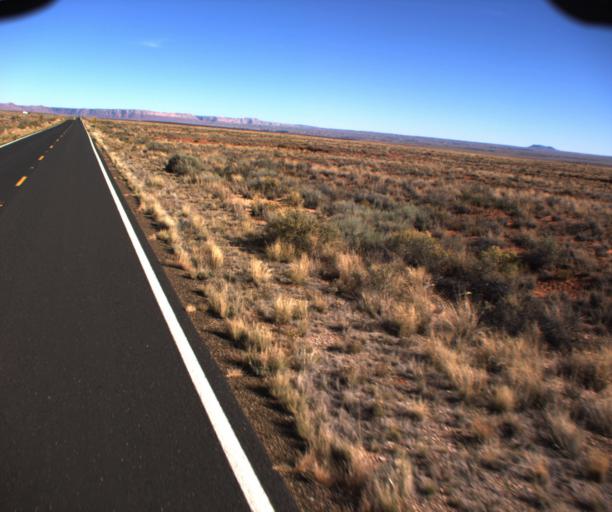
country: US
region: Arizona
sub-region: Coconino County
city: Page
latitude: 36.6994
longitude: -111.9234
